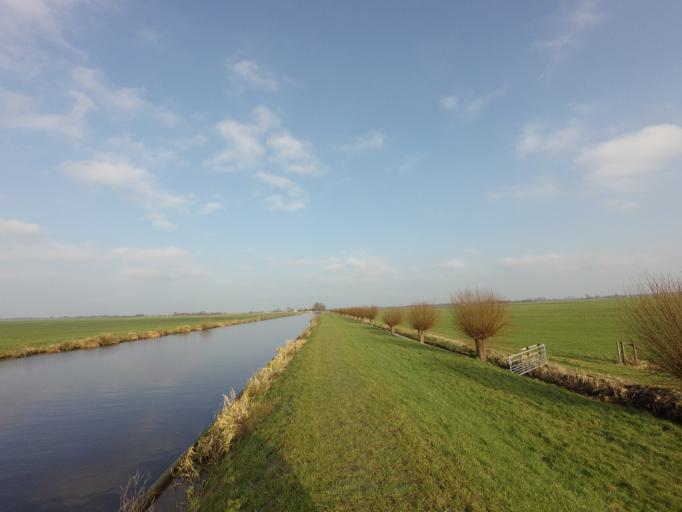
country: NL
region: Utrecht
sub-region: Gemeente Woerden
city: Woerden
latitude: 52.0982
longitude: 4.8665
